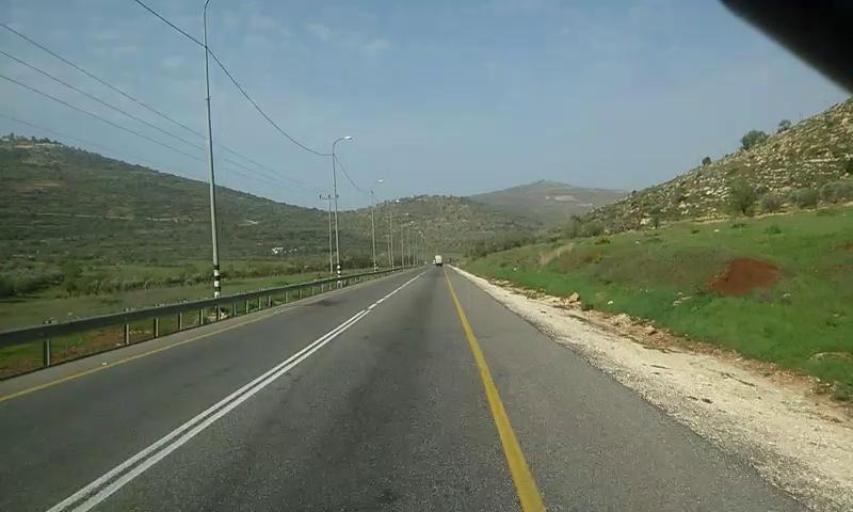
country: PS
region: West Bank
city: Al Lubban ash Sharqiyah
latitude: 32.0628
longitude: 35.2507
